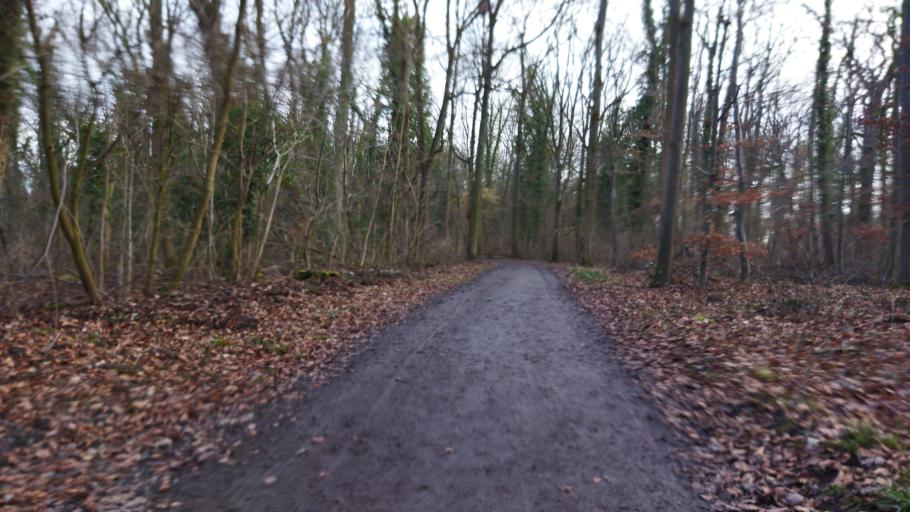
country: DE
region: Baden-Wuerttemberg
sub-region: Regierungsbezirk Stuttgart
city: Hessigheim
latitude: 48.9866
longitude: 9.1688
